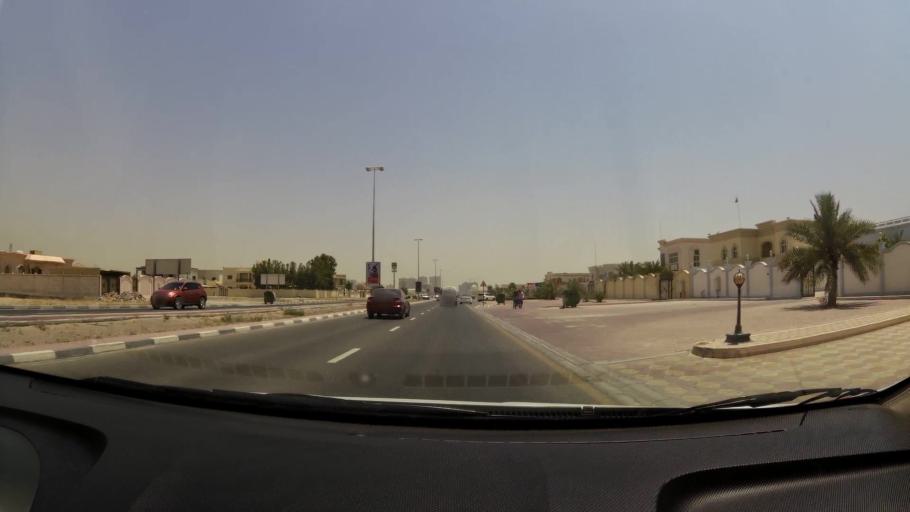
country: AE
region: Ajman
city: Ajman
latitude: 25.4177
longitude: 55.5133
